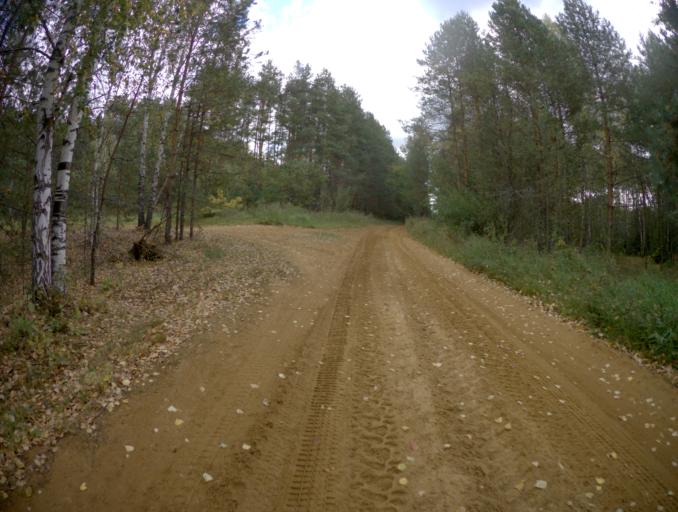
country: RU
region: Vladimir
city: Petushki
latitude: 55.8841
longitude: 39.5226
